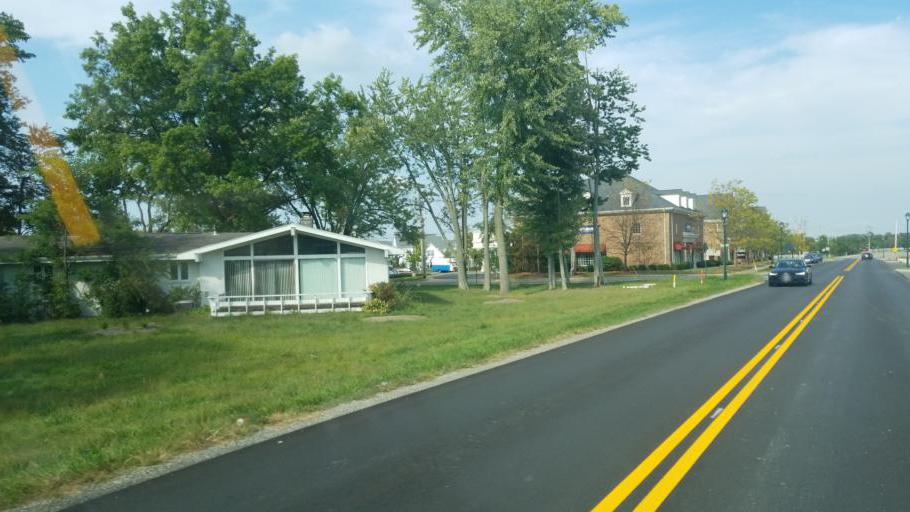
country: US
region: Ohio
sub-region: Franklin County
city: New Albany
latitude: 40.0838
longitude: -82.8051
